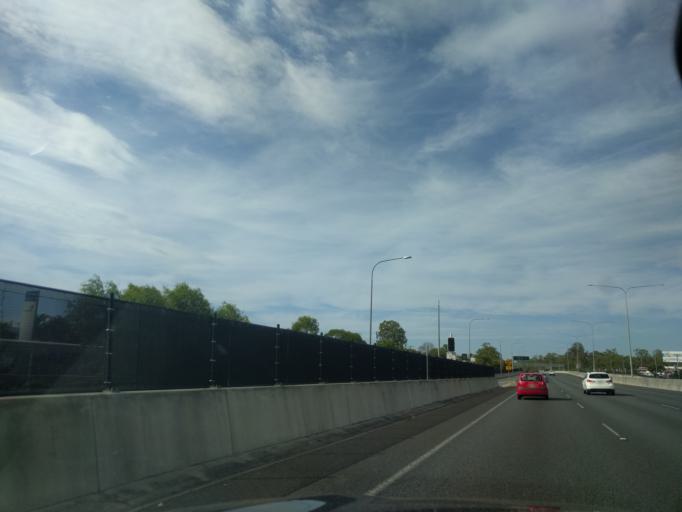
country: AU
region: Queensland
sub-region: Brisbane
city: Wacol
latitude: -27.5911
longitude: 152.9253
